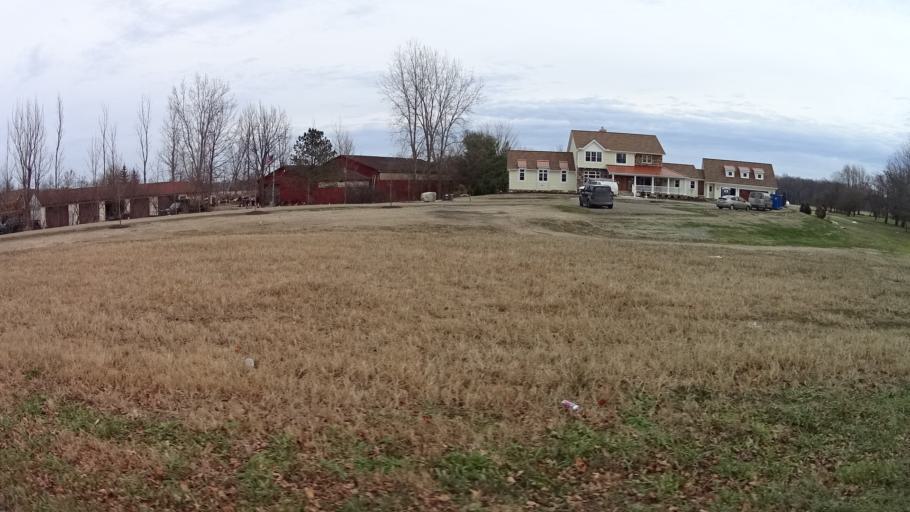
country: US
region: Ohio
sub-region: Lorain County
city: North Ridgeville
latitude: 41.4053
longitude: -82.0341
